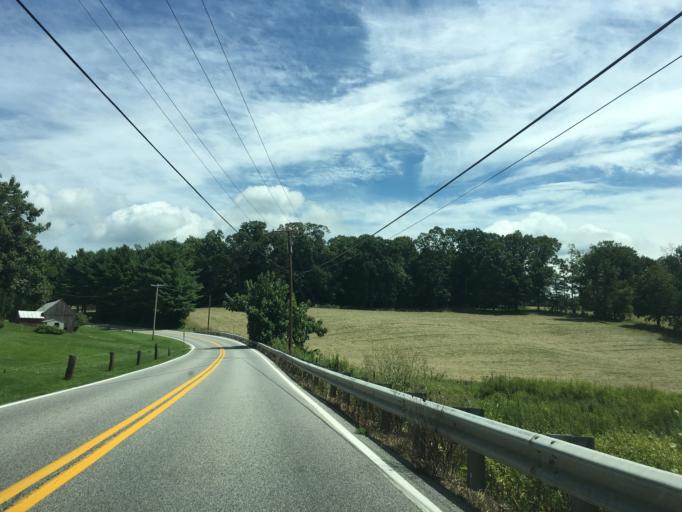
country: US
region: Pennsylvania
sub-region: York County
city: New Freedom
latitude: 39.7095
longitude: -76.6748
